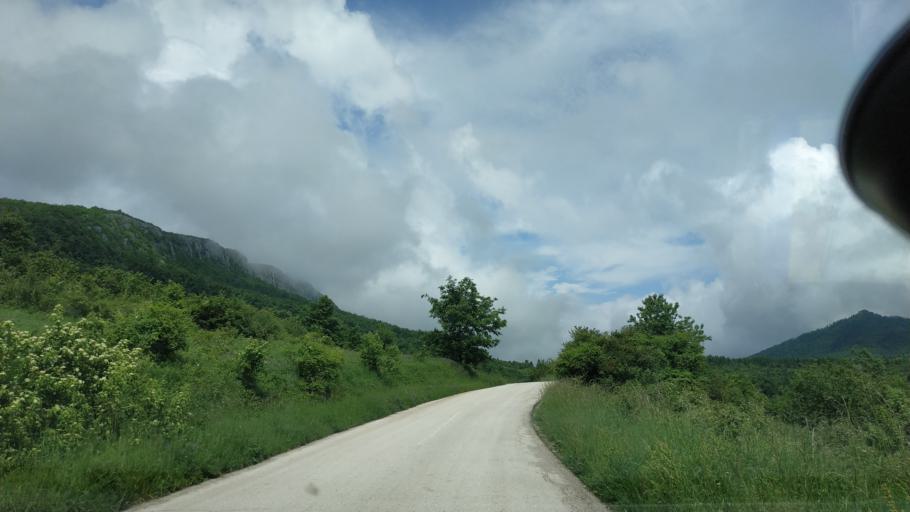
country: RS
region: Central Serbia
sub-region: Zajecarski Okrug
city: Boljevac
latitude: 43.7489
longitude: 21.9460
